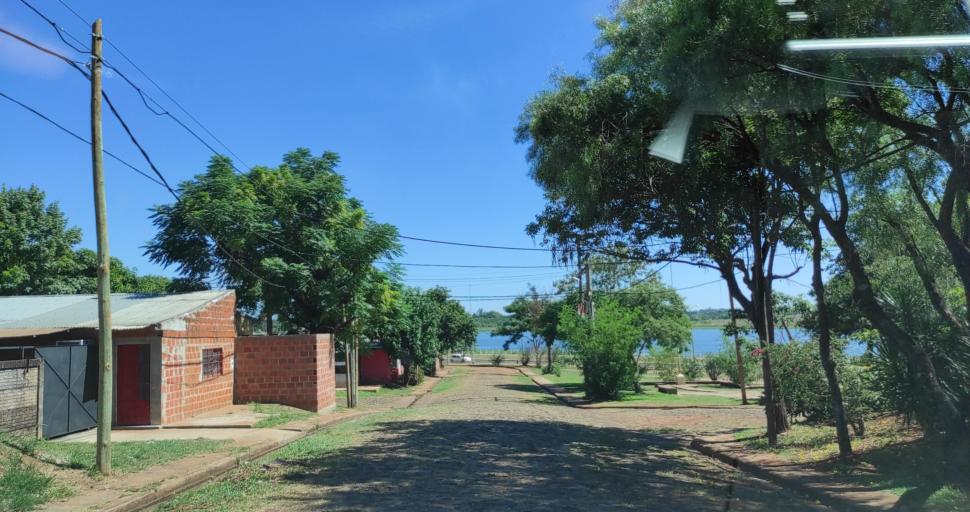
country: AR
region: Misiones
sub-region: Departamento de Capital
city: Posadas
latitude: -27.3839
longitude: -55.9511
